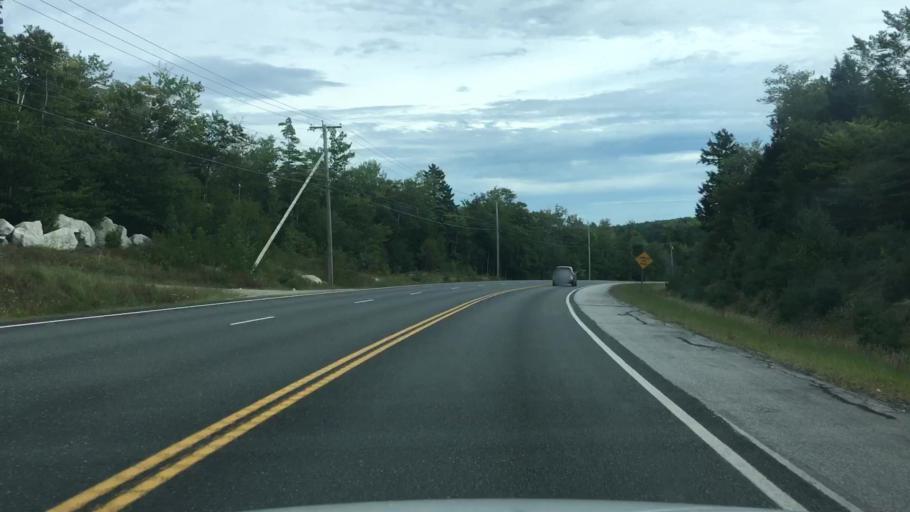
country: US
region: Maine
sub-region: Hancock County
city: Dedham
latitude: 44.6672
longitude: -68.5693
